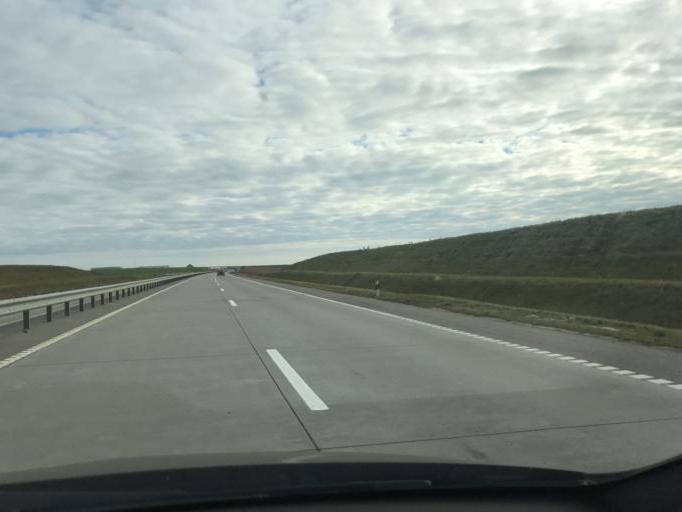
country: BY
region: Minsk
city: Syomkava
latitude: 54.0667
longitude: 27.4814
